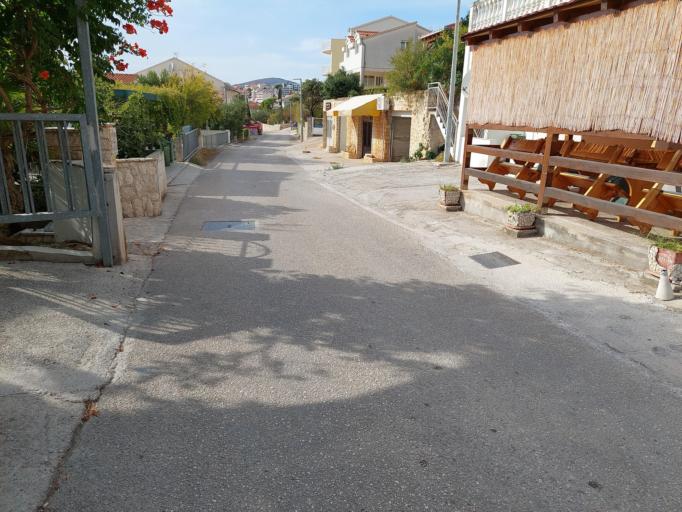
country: HR
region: Splitsko-Dalmatinska
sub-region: Grad Trogir
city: Trogir
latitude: 43.4913
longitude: 16.2782
